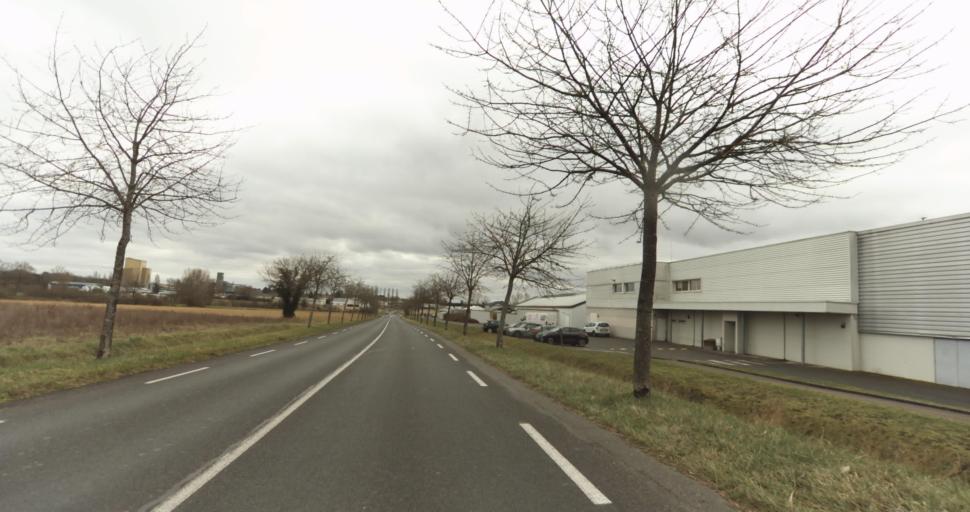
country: FR
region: Pays de la Loire
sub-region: Departement de Maine-et-Loire
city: Saint-Philbert-du-Peuple
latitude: 47.3735
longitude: -0.0988
